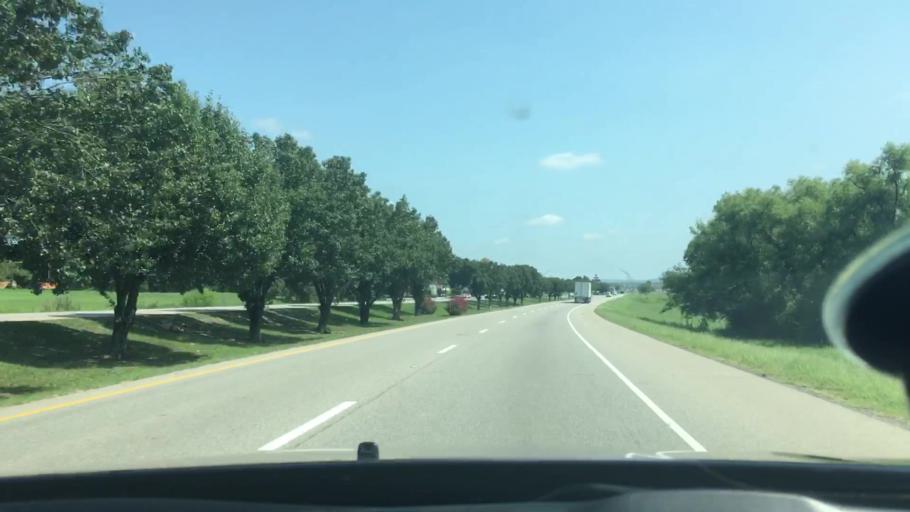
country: US
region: Oklahoma
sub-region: Atoka County
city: Atoka
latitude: 34.3574
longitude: -96.1463
